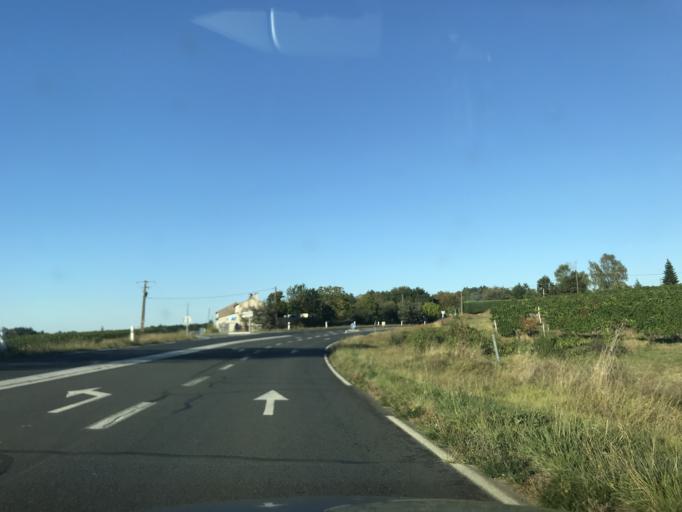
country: FR
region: Aquitaine
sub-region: Departement de la Gironde
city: Sauveterre-de-Guyenne
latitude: 44.6496
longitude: -0.1227
